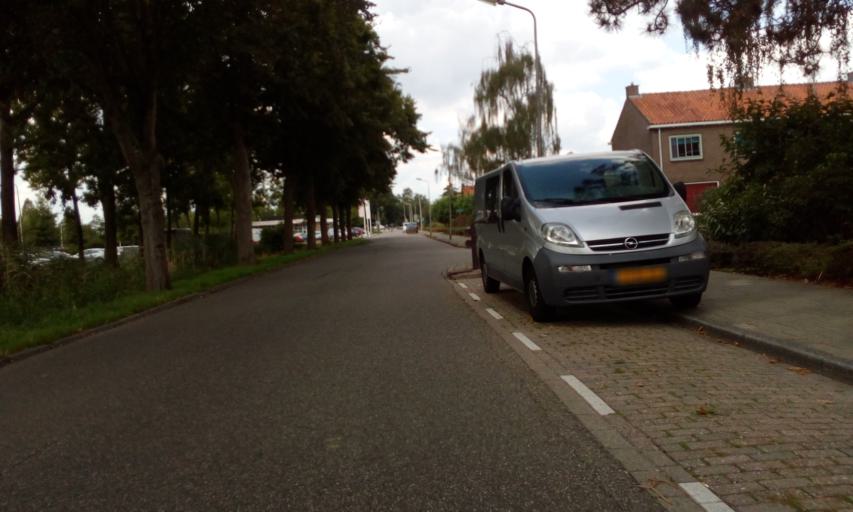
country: NL
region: South Holland
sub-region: Gemeente Waddinxveen
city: Waddinxveen
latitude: 52.0418
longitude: 4.6455
